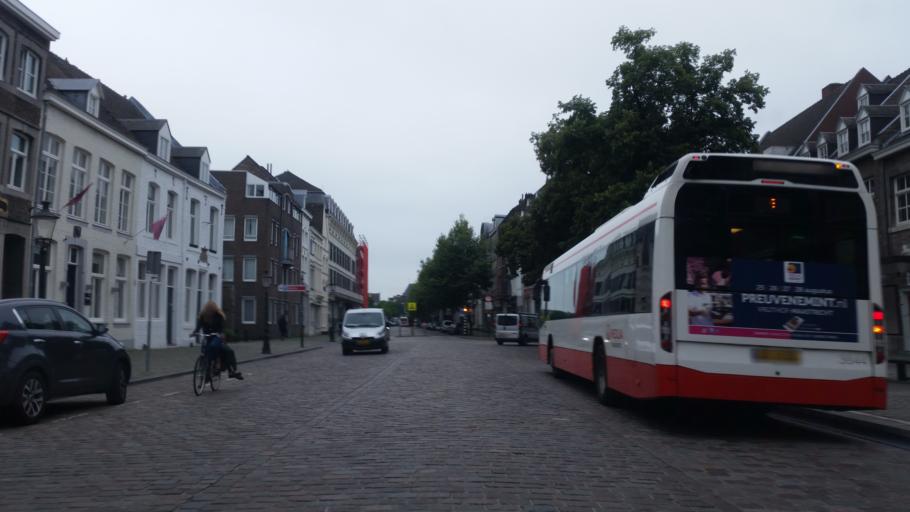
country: NL
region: Limburg
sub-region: Gemeente Maastricht
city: Maastricht
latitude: 50.8547
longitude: 5.6900
